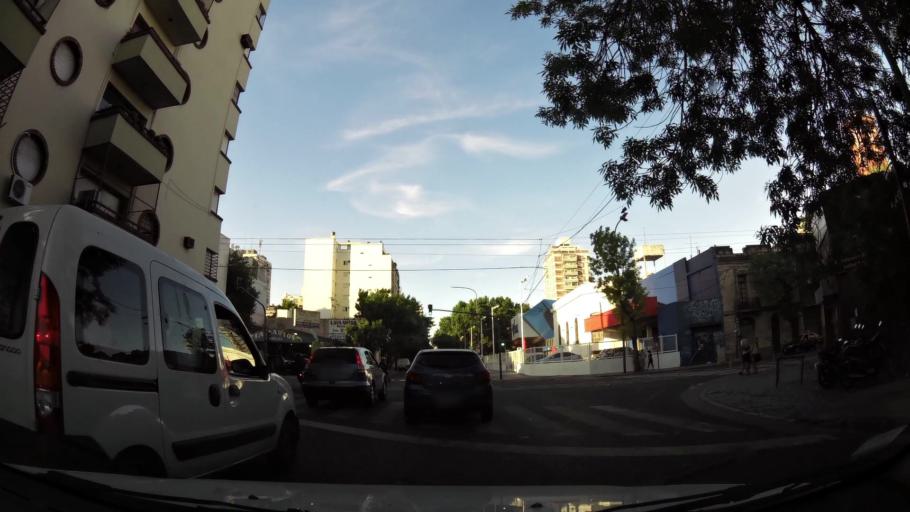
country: AR
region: Buenos Aires F.D.
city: Buenos Aires
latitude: -34.6075
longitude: -58.4140
